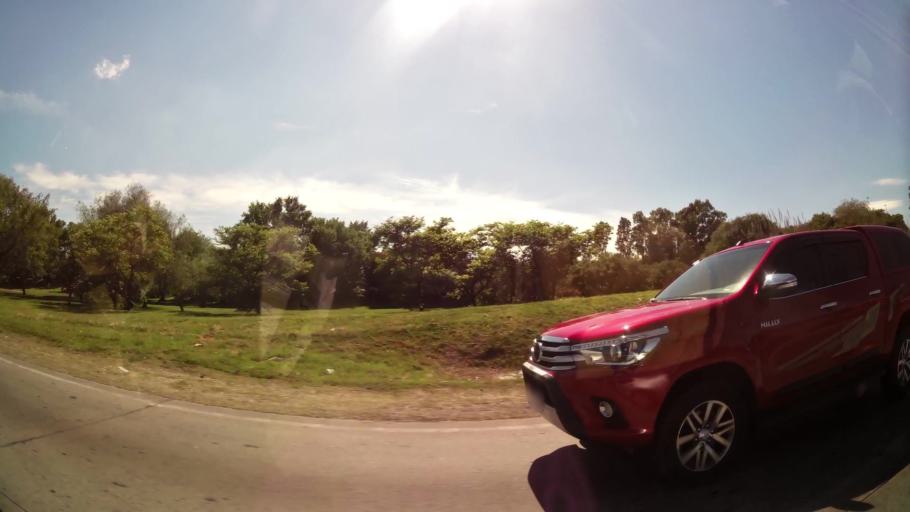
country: AR
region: Buenos Aires
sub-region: Partido de Tigre
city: Tigre
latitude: -34.4646
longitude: -58.5705
